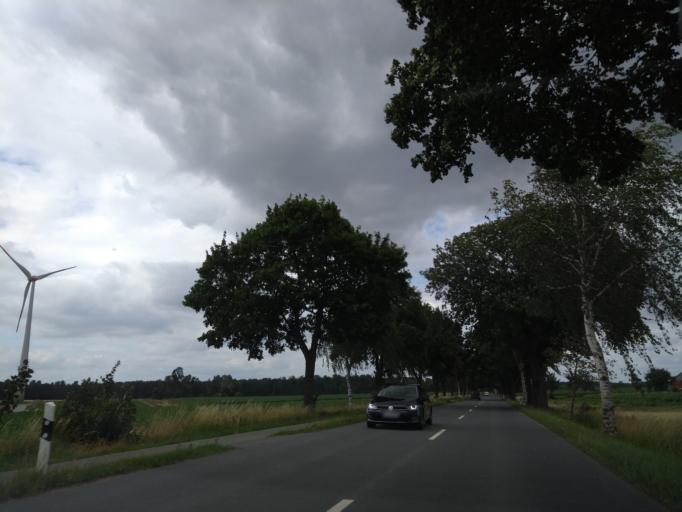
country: DE
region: North Rhine-Westphalia
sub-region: Regierungsbezirk Detmold
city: Salzkotten
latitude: 51.6512
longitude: 8.6684
